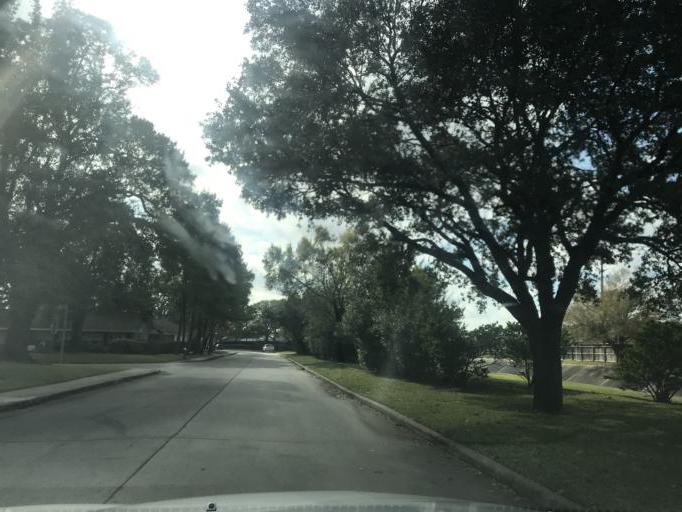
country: US
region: Texas
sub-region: Harris County
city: Piney Point Village
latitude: 29.7405
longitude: -95.4955
